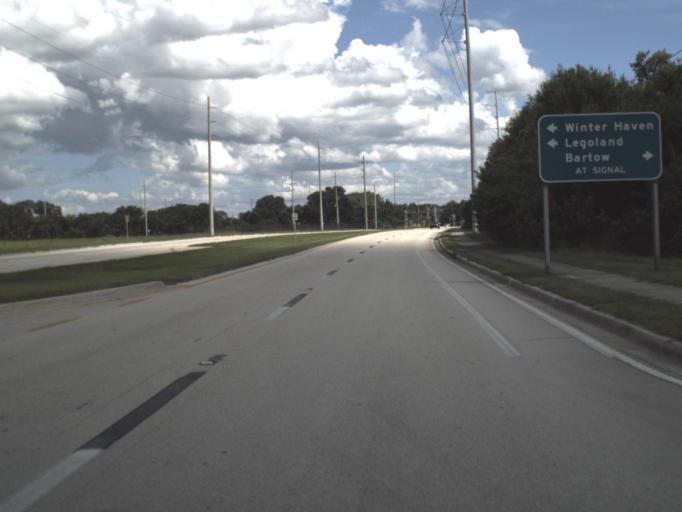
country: US
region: Florida
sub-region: Polk County
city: Eagle Lake
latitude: 27.9888
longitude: -81.7514
